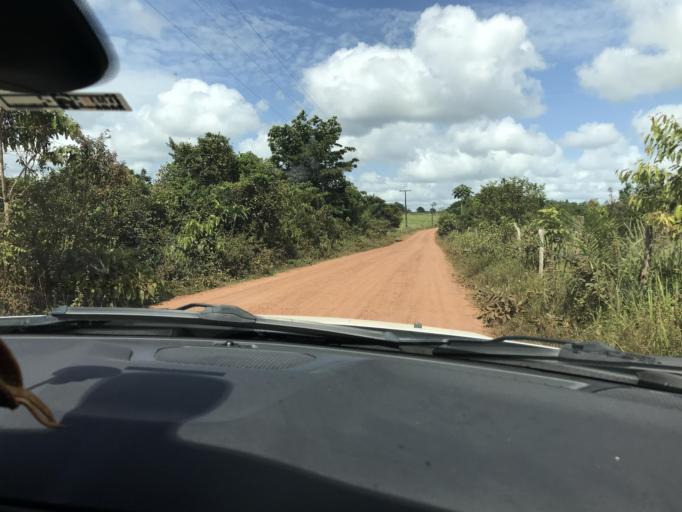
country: BR
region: Bahia
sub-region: Entre Rios
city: Entre Rios
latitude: -12.1871
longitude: -38.0503
